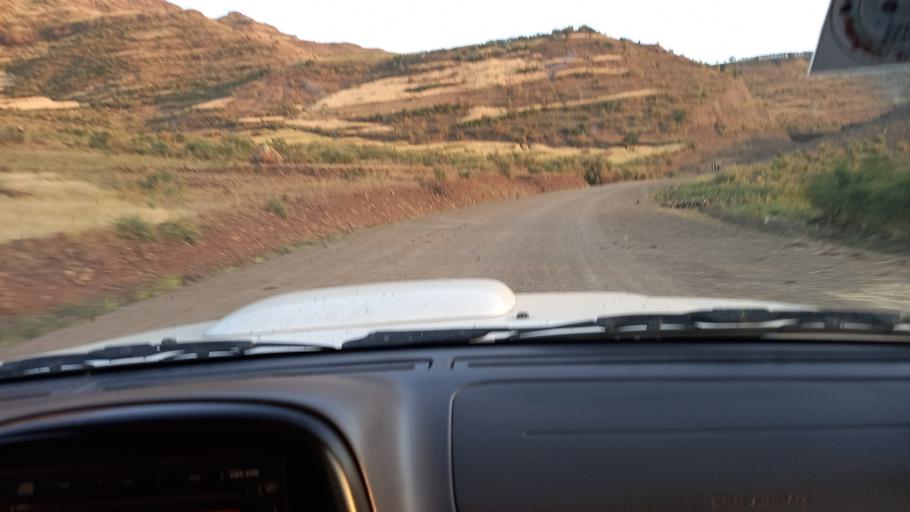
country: ET
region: Amhara
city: Debark'
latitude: 13.0528
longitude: 38.0194
